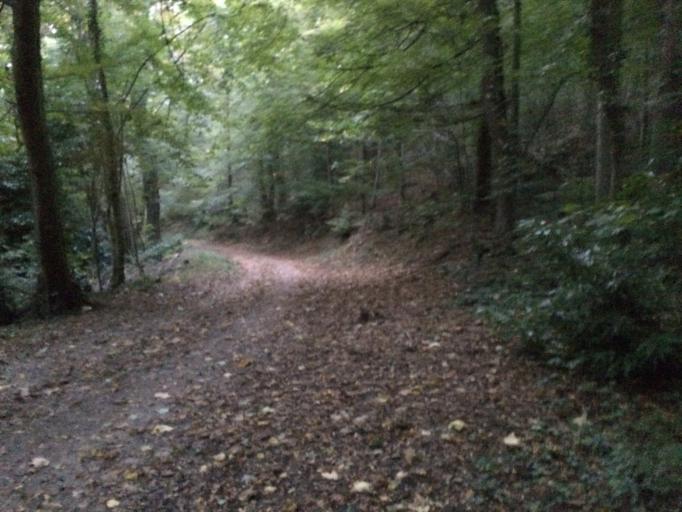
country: FR
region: Ile-de-France
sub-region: Departement des Yvelines
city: Velizy-Villacoublay
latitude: 48.7641
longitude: 2.1938
